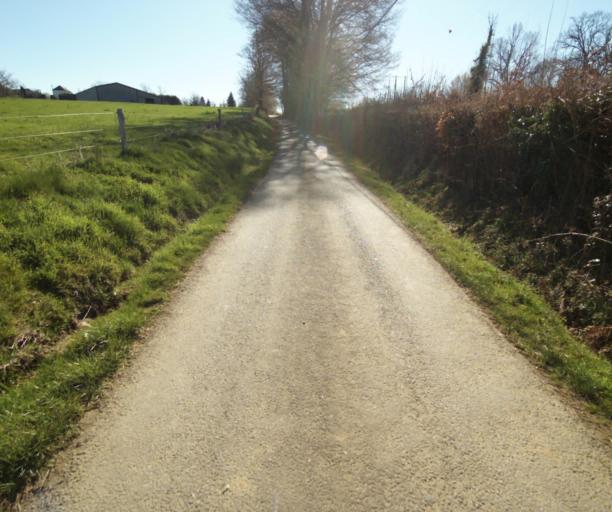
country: FR
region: Limousin
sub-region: Departement de la Correze
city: Chamboulive
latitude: 45.4069
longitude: 1.6986
